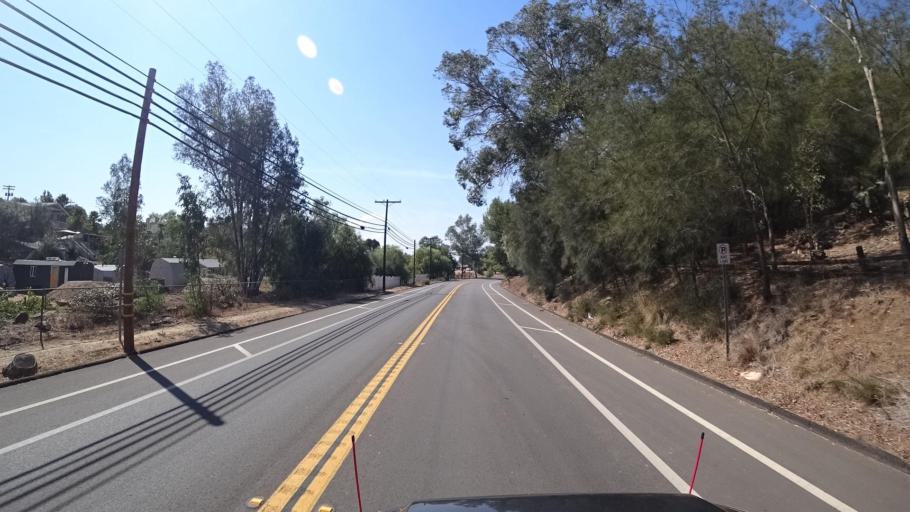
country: US
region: California
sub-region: San Diego County
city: Granite Hills
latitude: 32.7860
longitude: -116.9121
